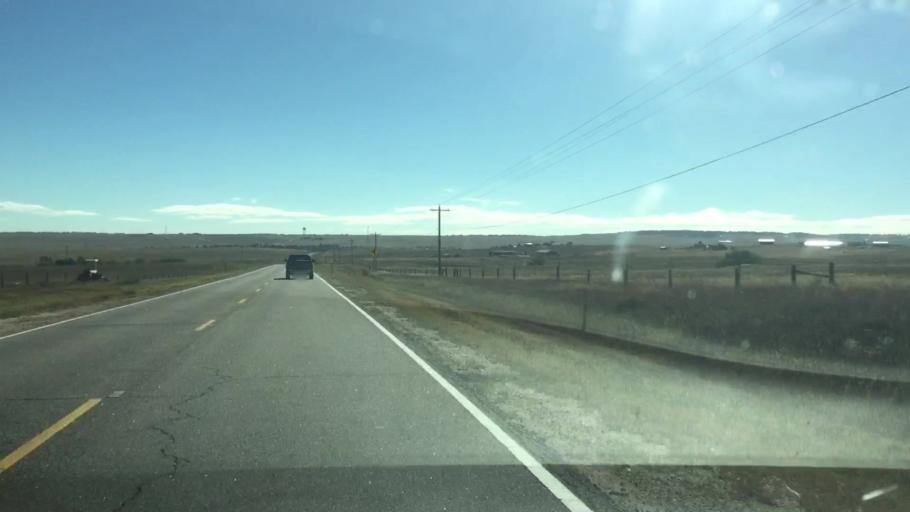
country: US
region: Colorado
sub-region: Elbert County
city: Kiowa
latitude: 39.3530
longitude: -104.5008
